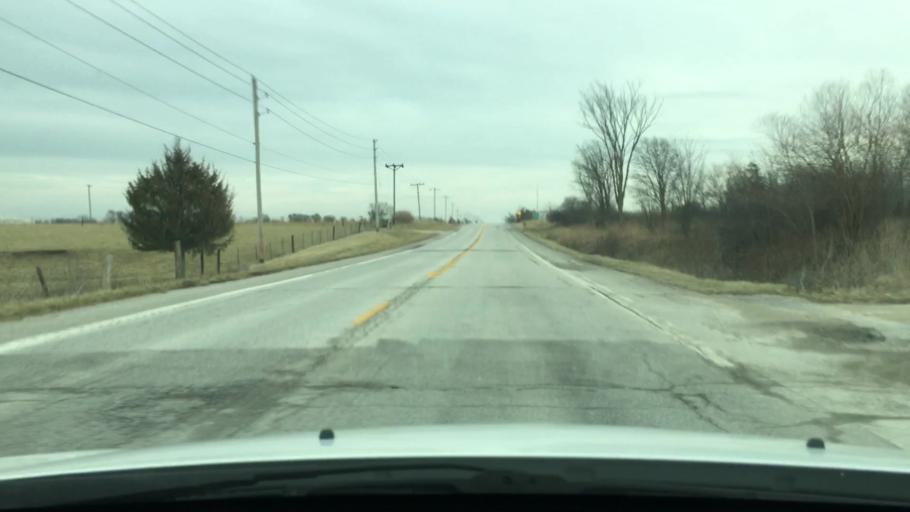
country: US
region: Missouri
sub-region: Pike County
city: Bowling Green
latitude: 39.3453
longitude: -91.3351
